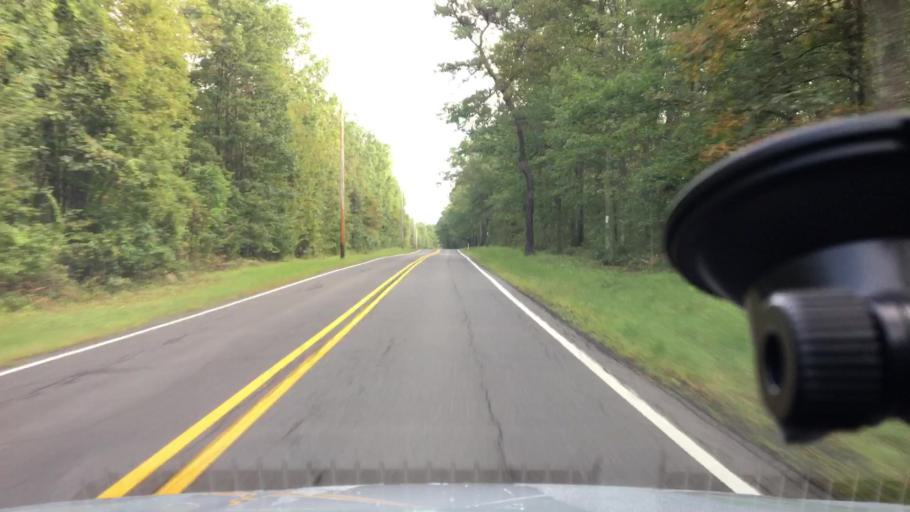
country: US
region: Pennsylvania
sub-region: Monroe County
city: Parkside
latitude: 41.1346
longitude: -75.2630
